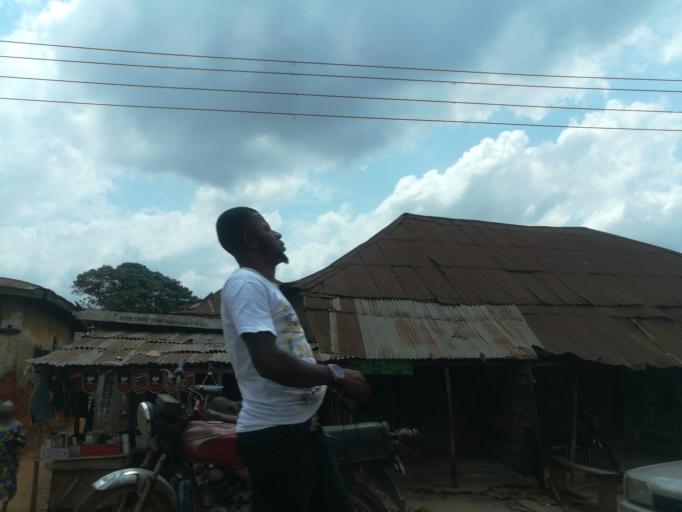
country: NG
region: Oyo
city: Ibadan
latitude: 7.3904
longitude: 3.9100
